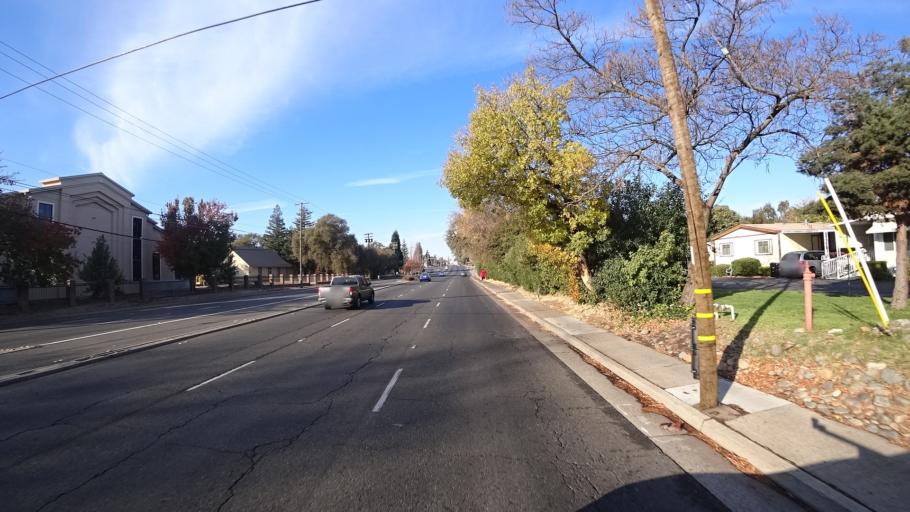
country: US
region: California
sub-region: Sacramento County
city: Foothill Farms
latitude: 38.6608
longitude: -121.3342
